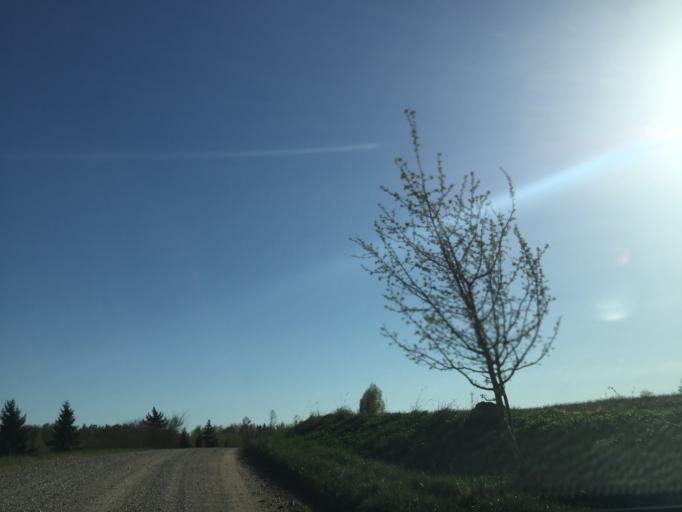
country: LV
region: Ergli
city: Ergli
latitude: 56.8962
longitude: 25.4946
